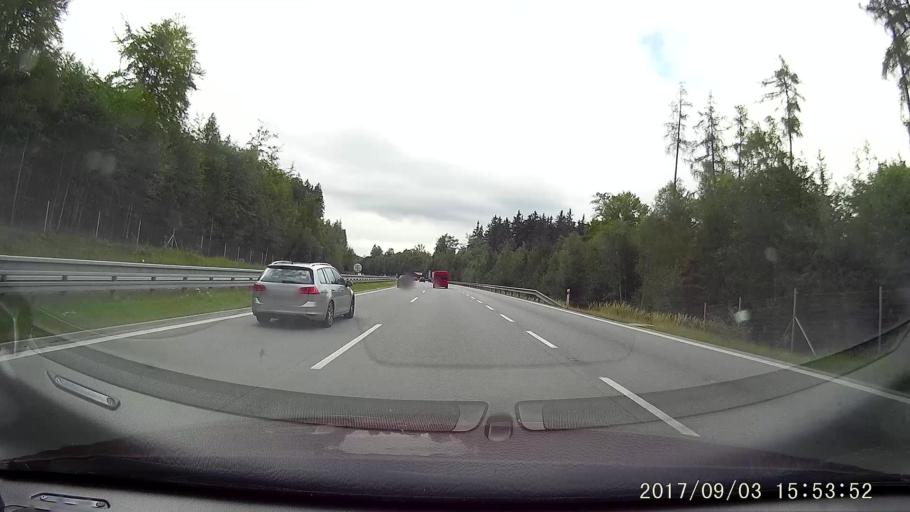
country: CZ
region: Vysocina
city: Stoky
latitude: 49.4640
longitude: 15.5798
